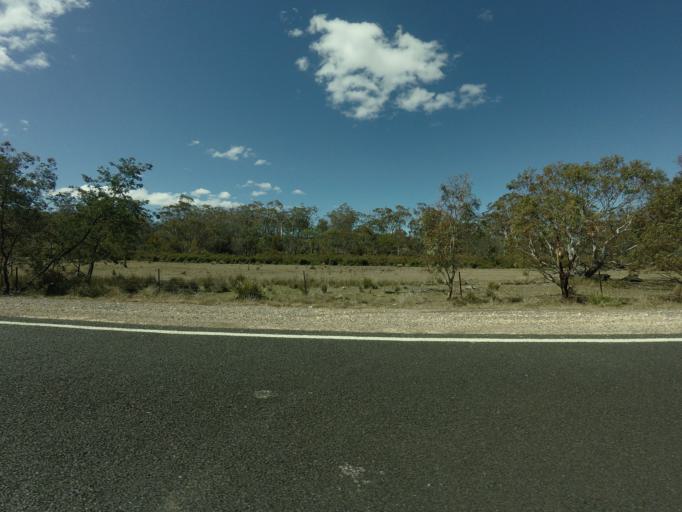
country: AU
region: Tasmania
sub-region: Break O'Day
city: St Helens
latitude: -42.0344
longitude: 148.0248
